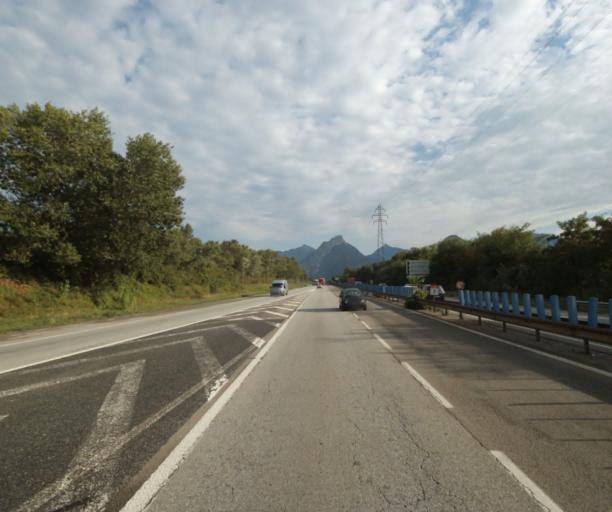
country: FR
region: Rhone-Alpes
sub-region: Departement de l'Isere
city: Grenoble
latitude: 45.1620
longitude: 5.7016
